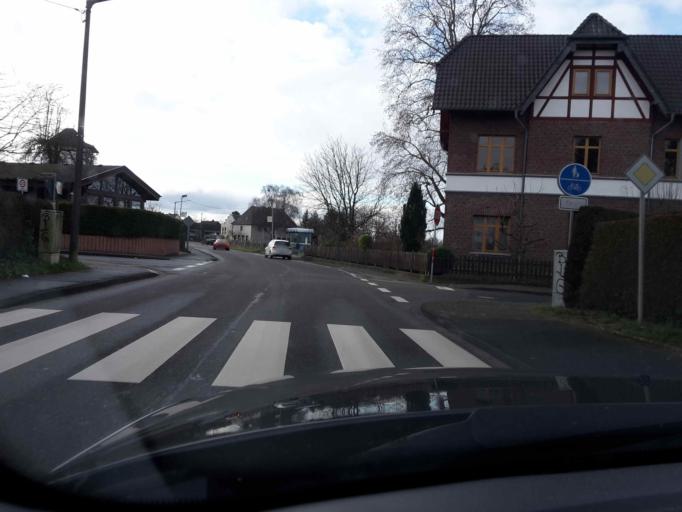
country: DE
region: North Rhine-Westphalia
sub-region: Regierungsbezirk Koln
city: Hennef
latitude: 50.7499
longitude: 7.2797
